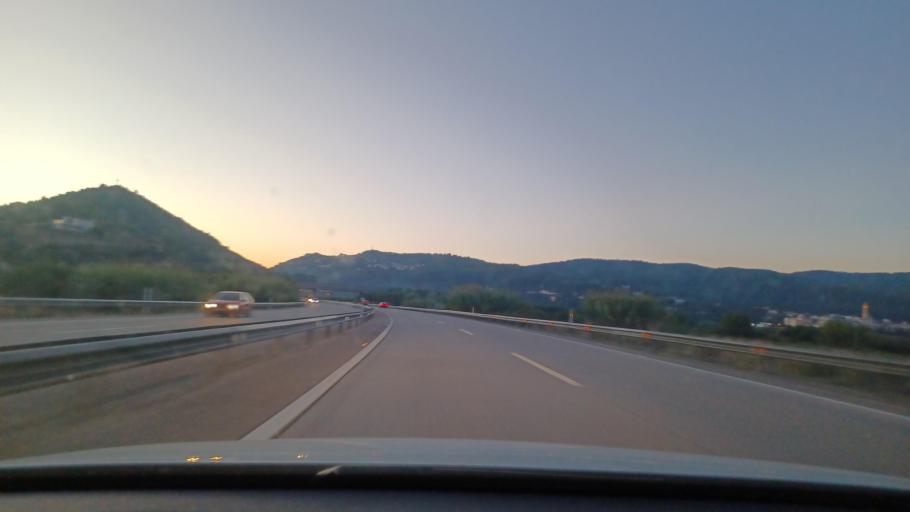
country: ES
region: Valencia
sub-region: Provincia de Valencia
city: Benifla
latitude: 38.9297
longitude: -0.1740
